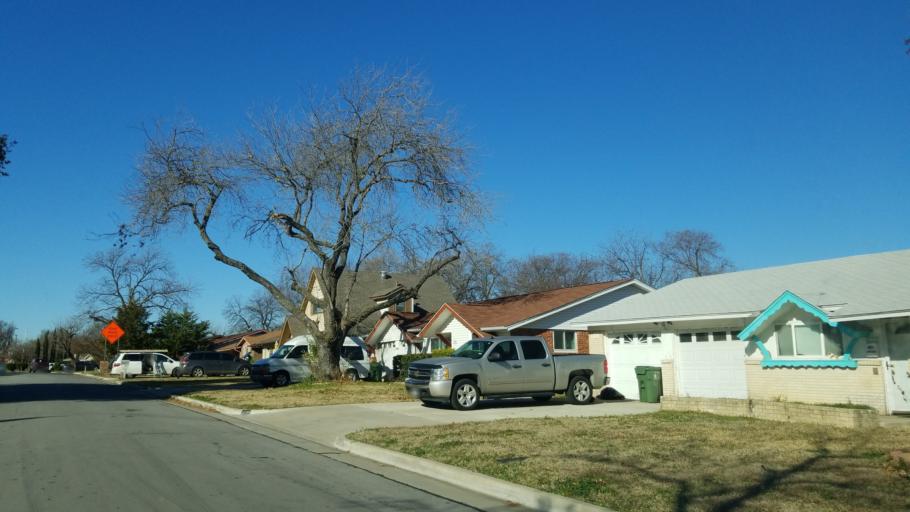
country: US
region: Texas
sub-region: Tarrant County
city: Arlington
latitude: 32.7268
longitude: -97.0600
